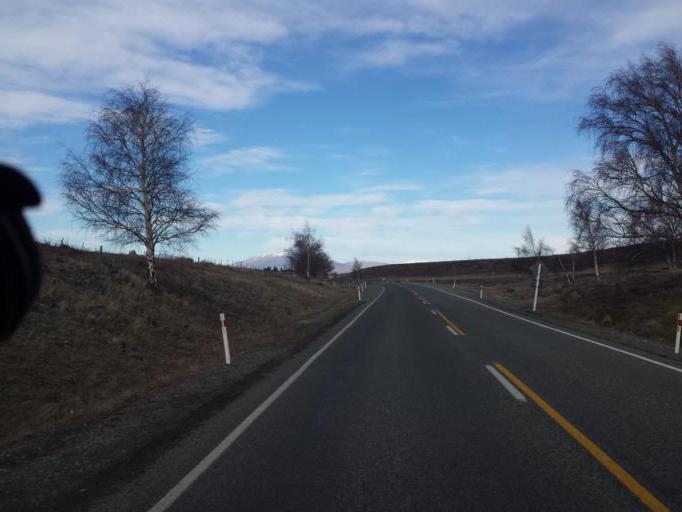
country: NZ
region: Canterbury
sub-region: Timaru District
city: Pleasant Point
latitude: -44.0169
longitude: 170.5009
